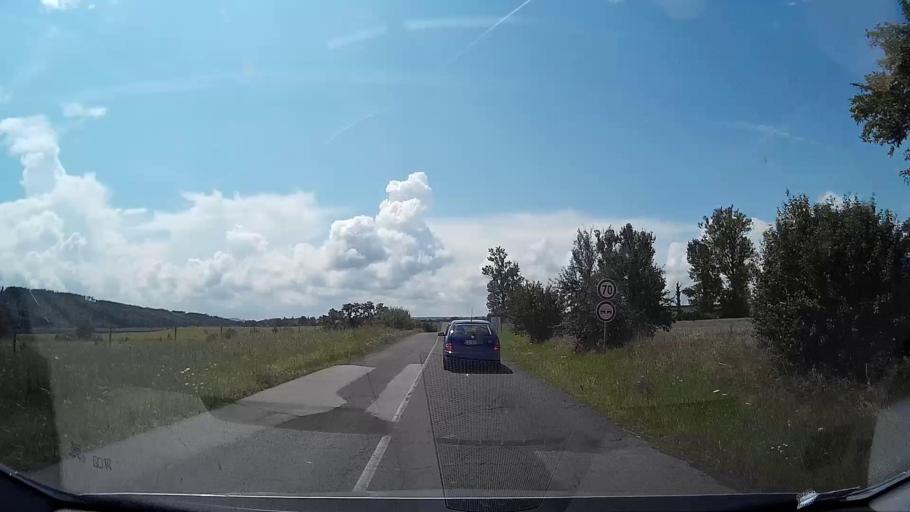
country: SK
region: Banskobystricky
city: Fil'akovo
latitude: 48.3337
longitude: 19.8208
